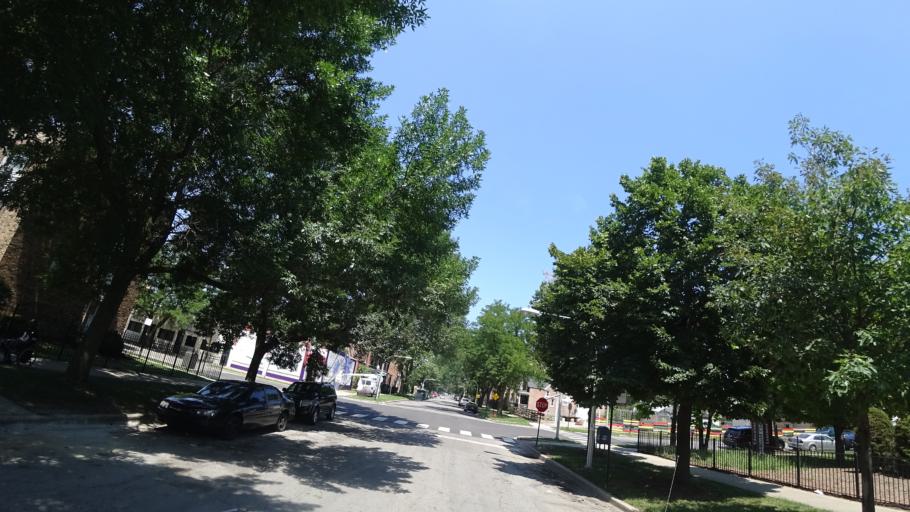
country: US
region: Illinois
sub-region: Cook County
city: Chicago
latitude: 41.7675
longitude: -87.5910
